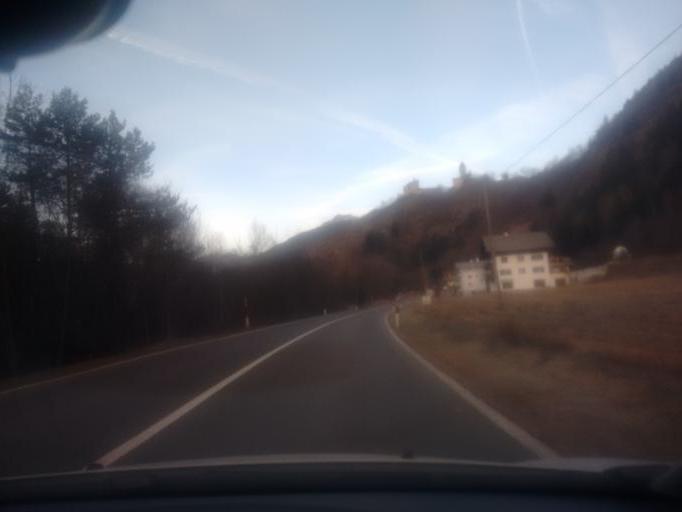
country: IT
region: Trentino-Alto Adige
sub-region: Bolzano
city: Prati
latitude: 46.8800
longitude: 11.4620
